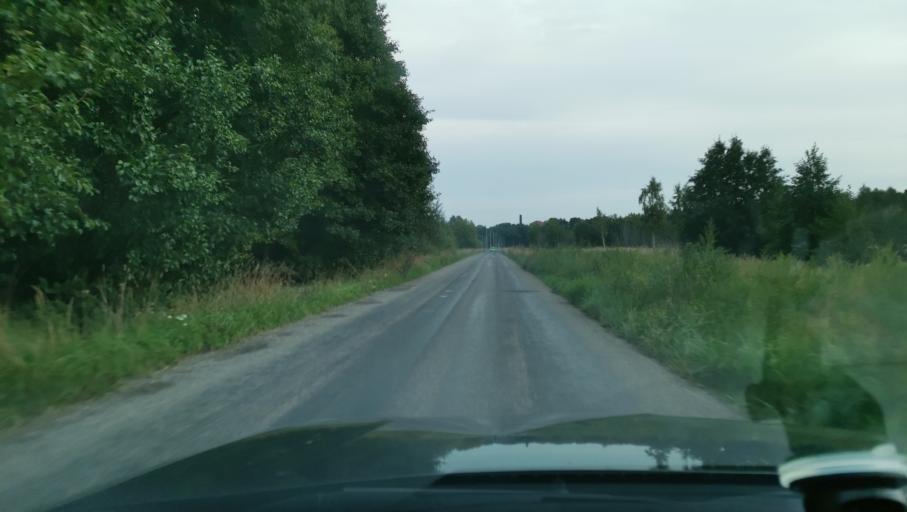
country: EE
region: Harju
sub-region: Saue vald
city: Laagri
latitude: 59.4218
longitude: 24.6270
